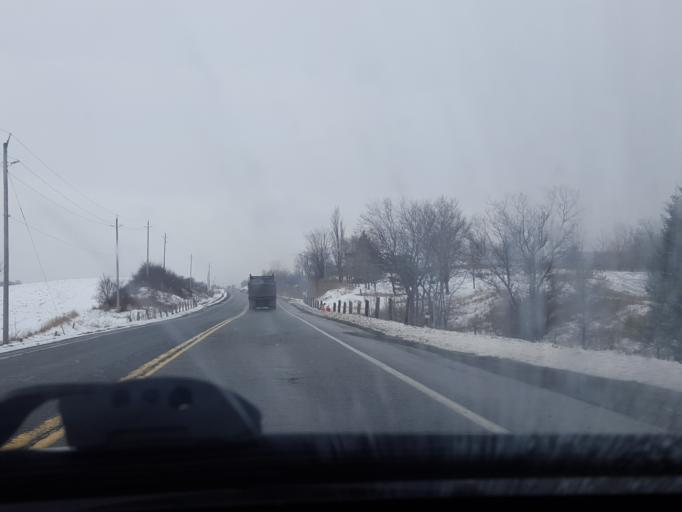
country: CA
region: Ontario
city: Newmarket
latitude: 43.9892
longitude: -79.3428
